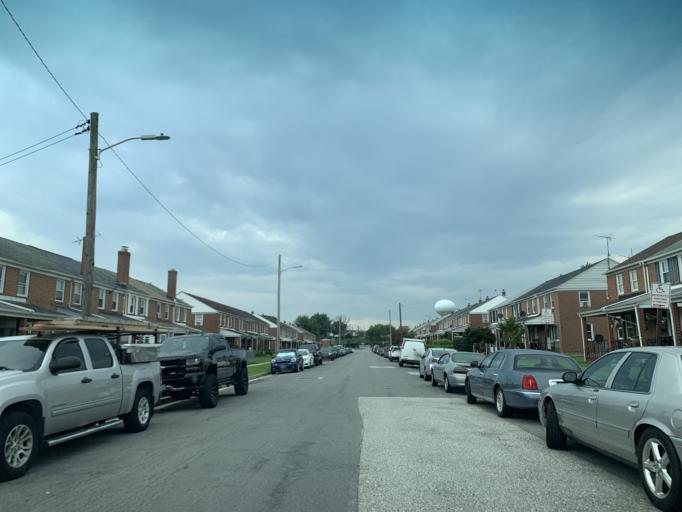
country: US
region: Maryland
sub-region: Baltimore County
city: Rosedale
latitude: 39.2928
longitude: -76.5227
